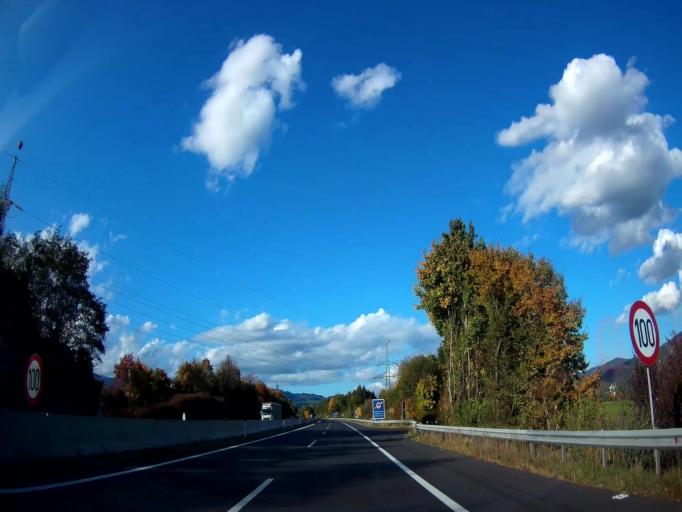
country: AT
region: Carinthia
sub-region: Politischer Bezirk Wolfsberg
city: Wolfsberg
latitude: 46.8158
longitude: 14.8228
